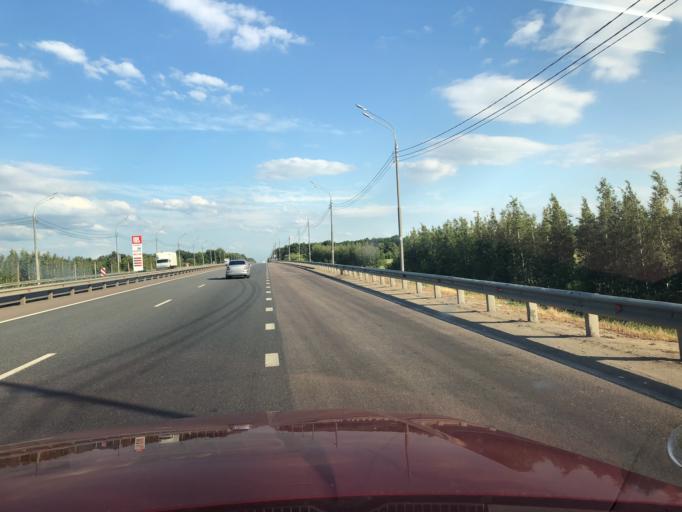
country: RU
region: Lipetsk
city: Zadonsk
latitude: 52.4257
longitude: 38.8299
